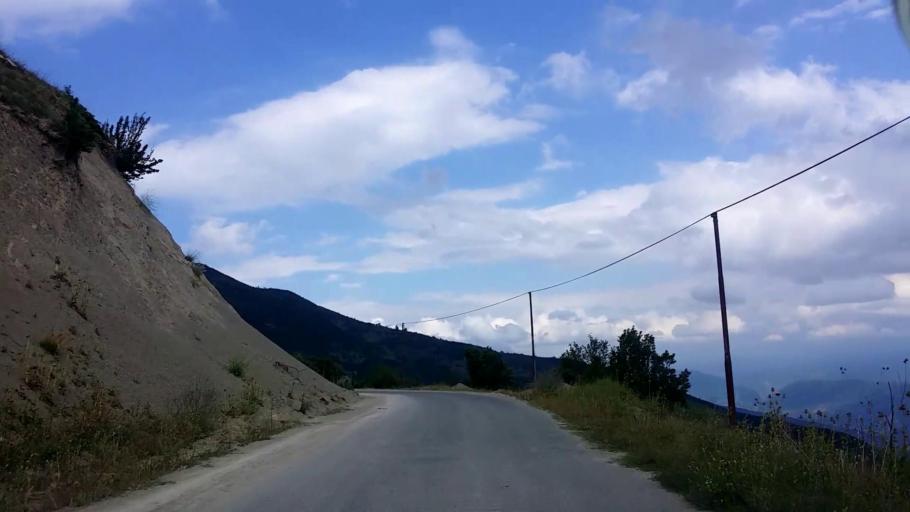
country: IR
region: Mazandaran
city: Chalus
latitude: 36.5526
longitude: 51.2840
